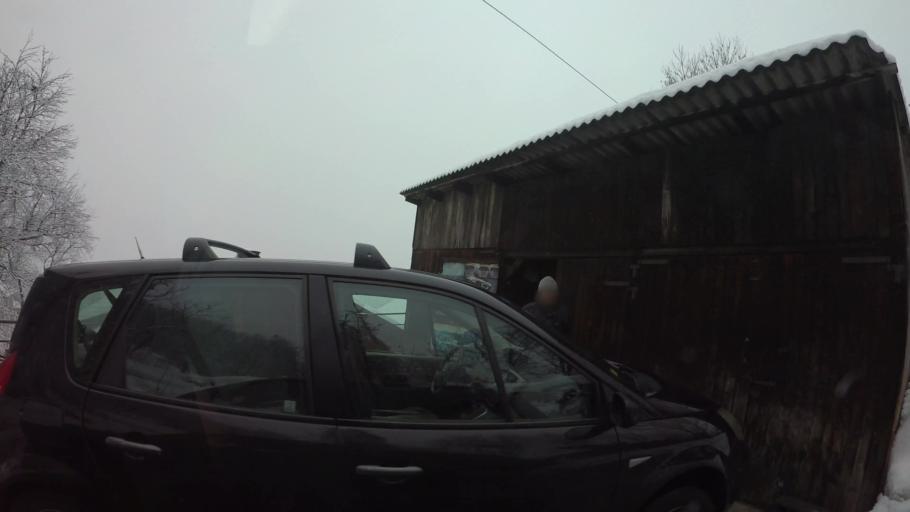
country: BA
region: Federation of Bosnia and Herzegovina
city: Kobilja Glava
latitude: 43.8476
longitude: 18.4185
